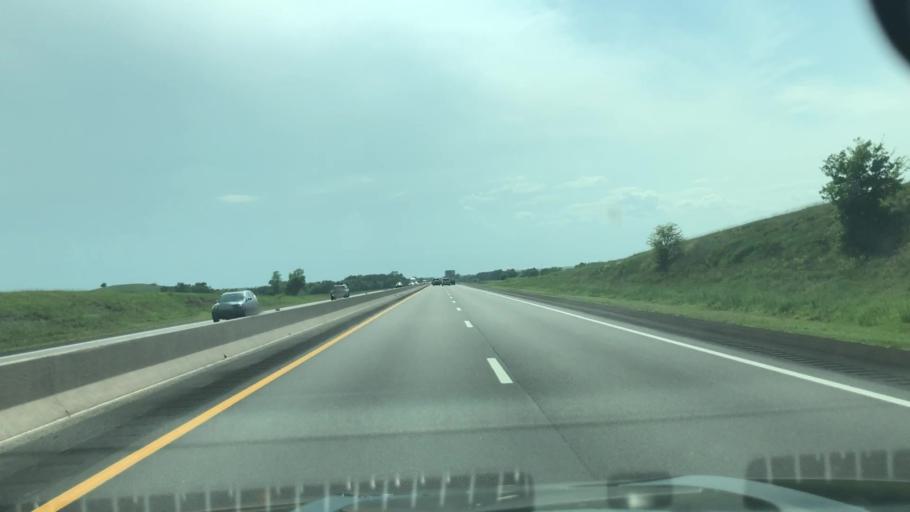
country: US
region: Oklahoma
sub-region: Ottawa County
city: Afton
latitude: 36.6918
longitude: -95.0156
